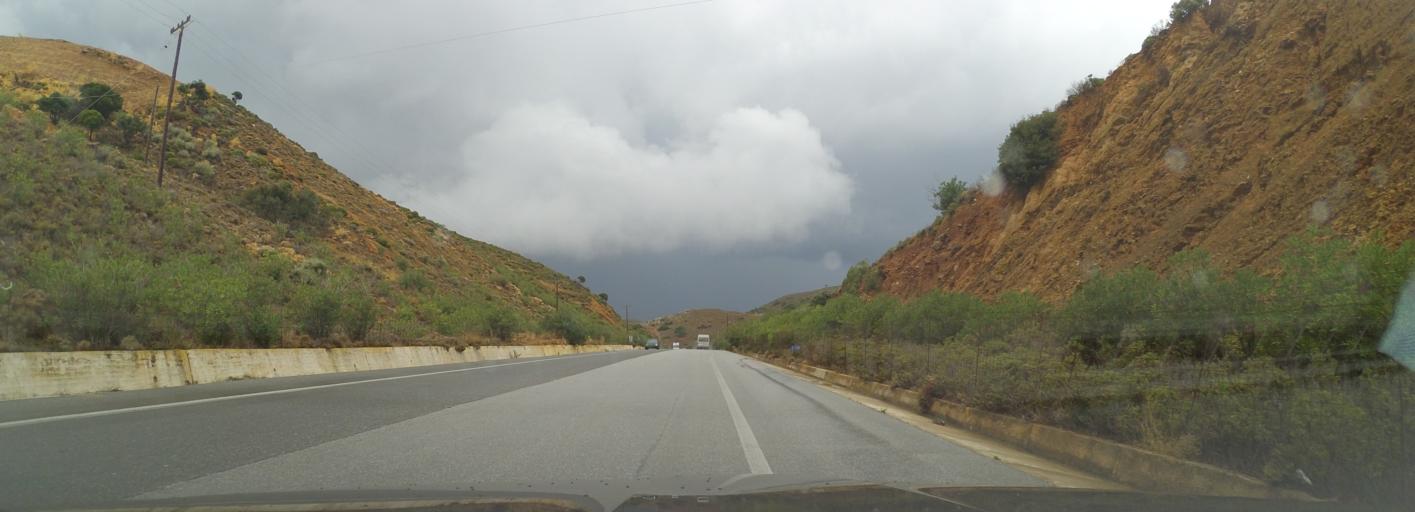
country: GR
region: Crete
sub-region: Nomos Rethymnis
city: Anogeia
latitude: 35.3911
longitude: 24.9286
